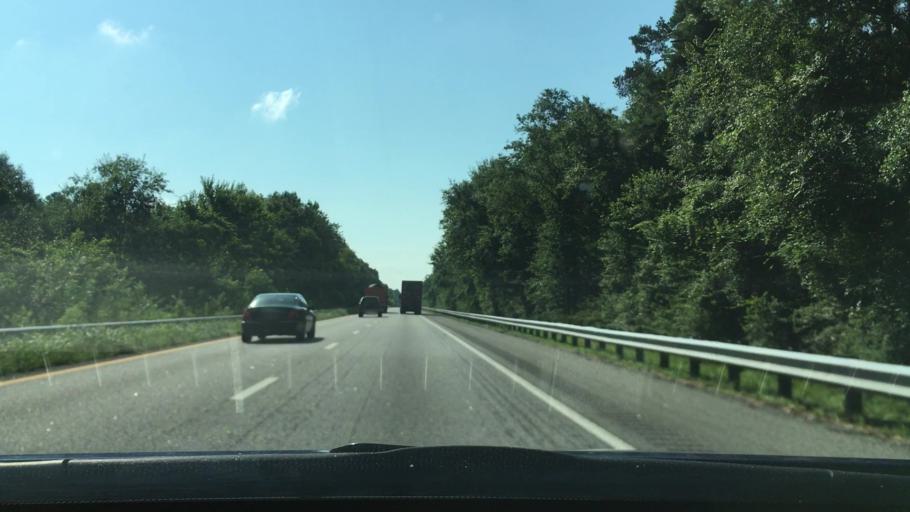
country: US
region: South Carolina
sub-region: Dorchester County
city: Ridgeville
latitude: 33.1494
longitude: -80.3362
